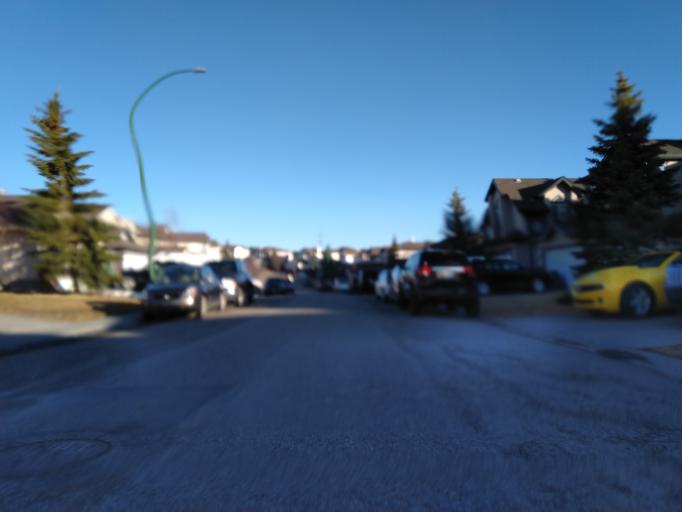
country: CA
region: Alberta
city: Cochrane
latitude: 51.1844
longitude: -114.5104
